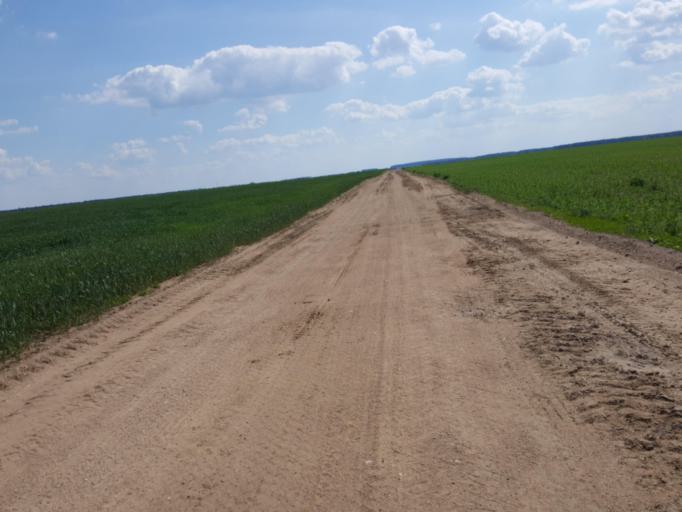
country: BY
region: Brest
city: Kamyanyuki
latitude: 52.4939
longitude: 23.6019
